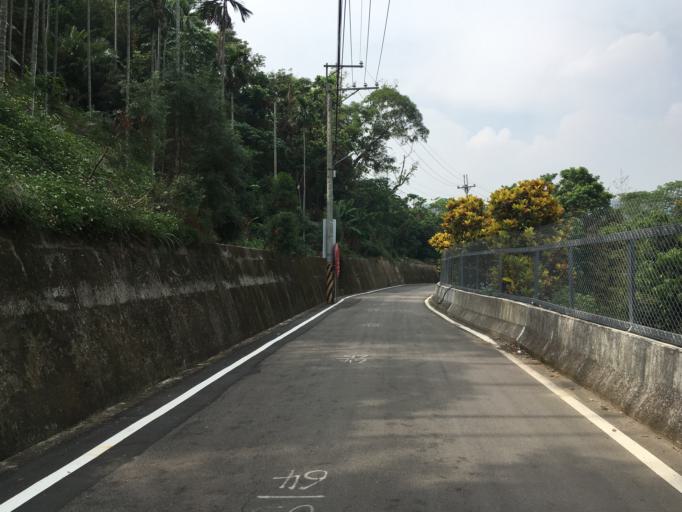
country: TW
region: Taiwan
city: Fengyuan
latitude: 24.1868
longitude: 120.7509
